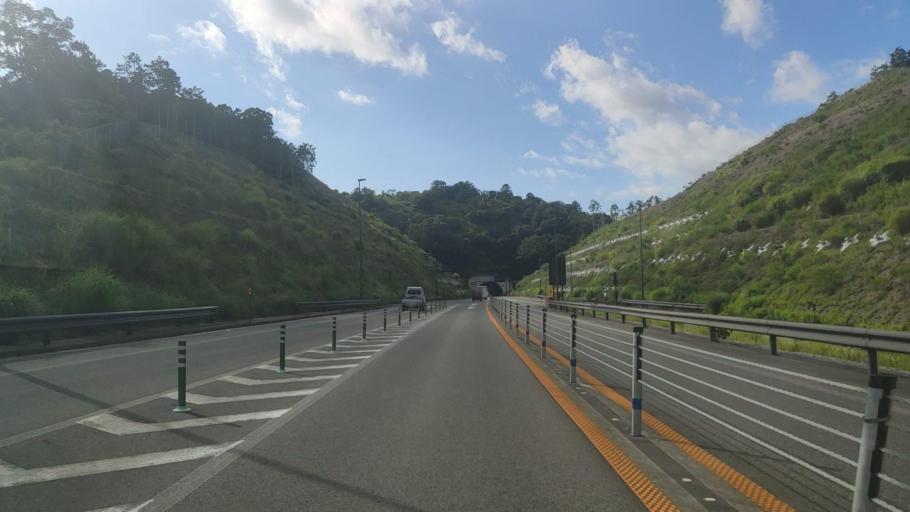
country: JP
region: Wakayama
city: Tanabe
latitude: 33.5807
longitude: 135.4535
